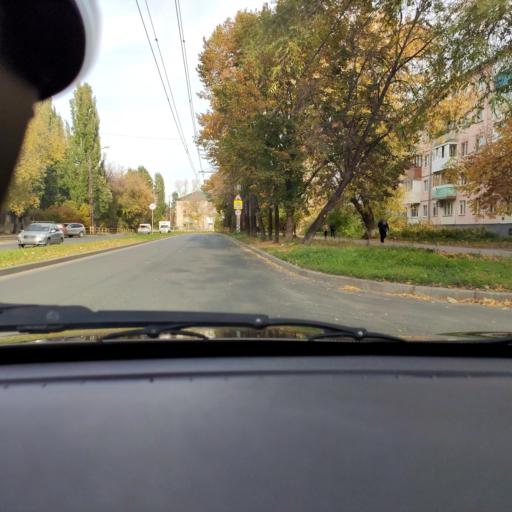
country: RU
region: Samara
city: Tol'yatti
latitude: 53.5209
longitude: 49.4099
